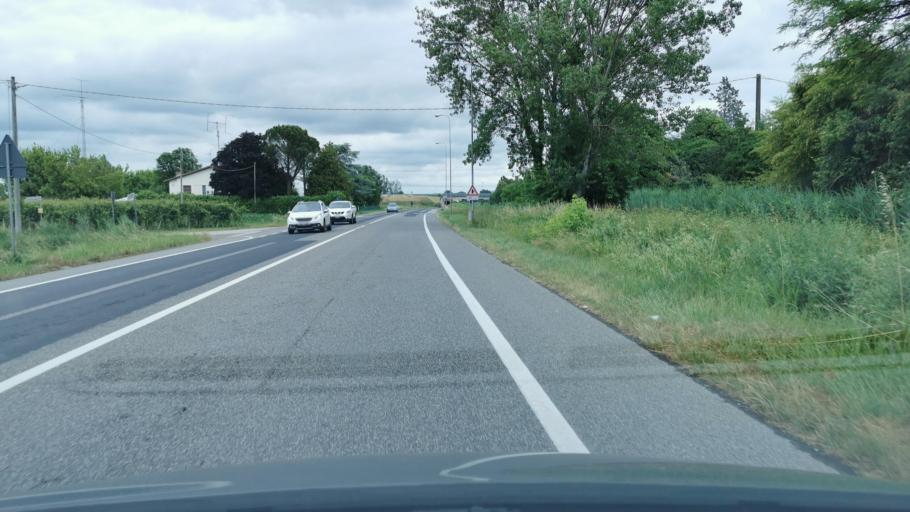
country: IT
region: Emilia-Romagna
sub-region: Provincia di Ravenna
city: Cotignola
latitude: 44.3959
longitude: 11.9590
